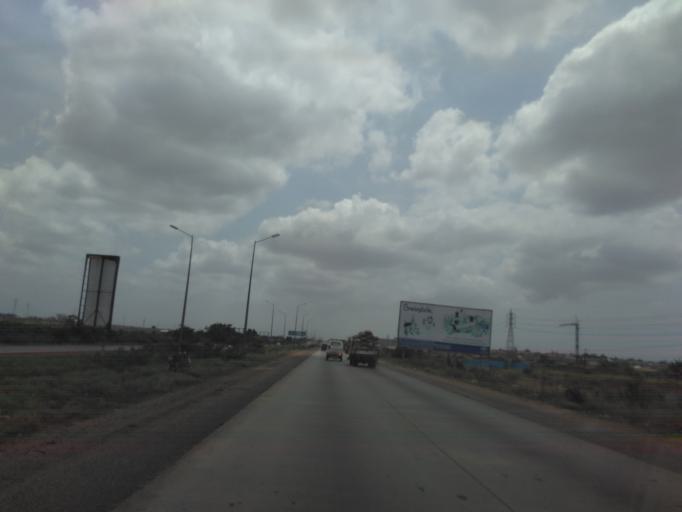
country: GH
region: Greater Accra
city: Tema
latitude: 5.6637
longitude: -0.0680
